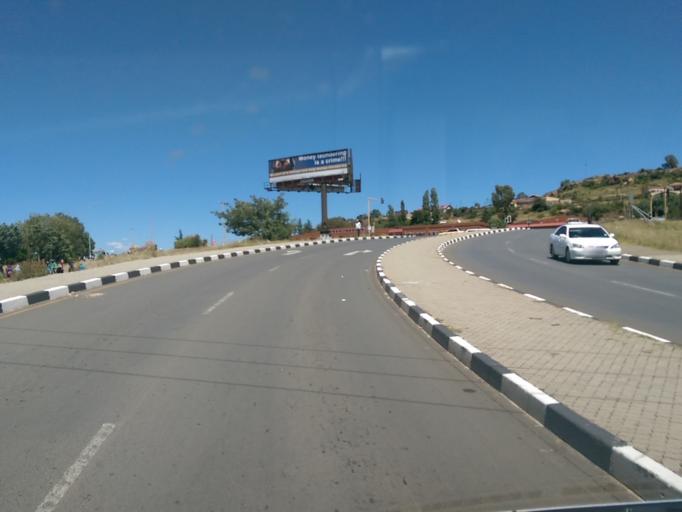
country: LS
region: Maseru
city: Maseru
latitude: -29.3245
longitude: 27.5005
